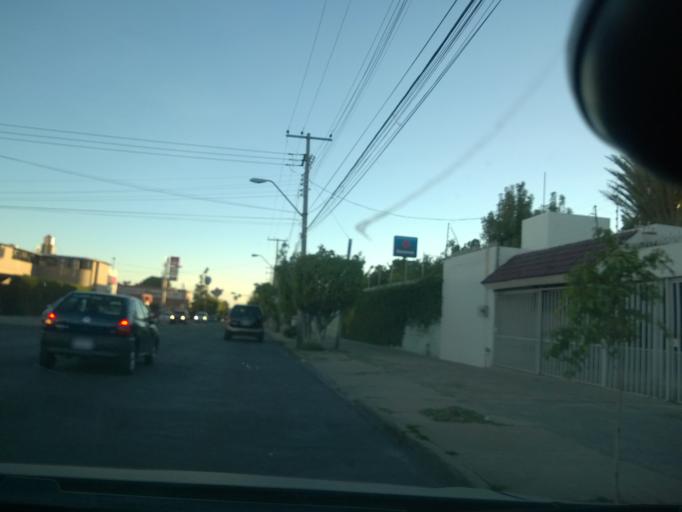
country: MX
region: Guanajuato
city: Leon
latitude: 21.1230
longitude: -101.6942
